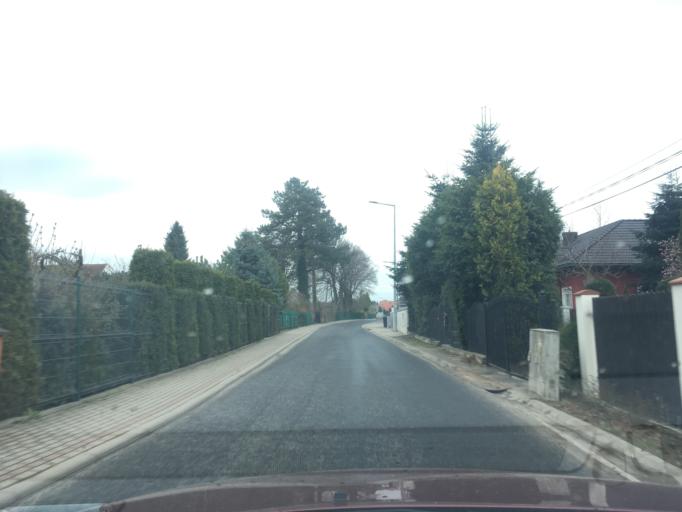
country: PL
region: Lower Silesian Voivodeship
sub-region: Powiat zgorzelecki
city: Lagow
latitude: 51.1561
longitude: 15.0428
